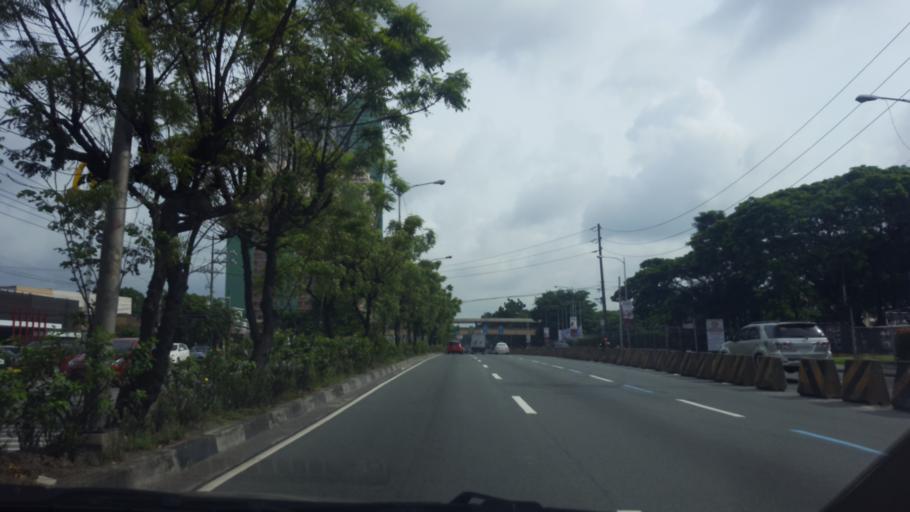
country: PH
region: Metro Manila
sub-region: Marikina
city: Calumpang
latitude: 14.6354
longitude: 121.0744
